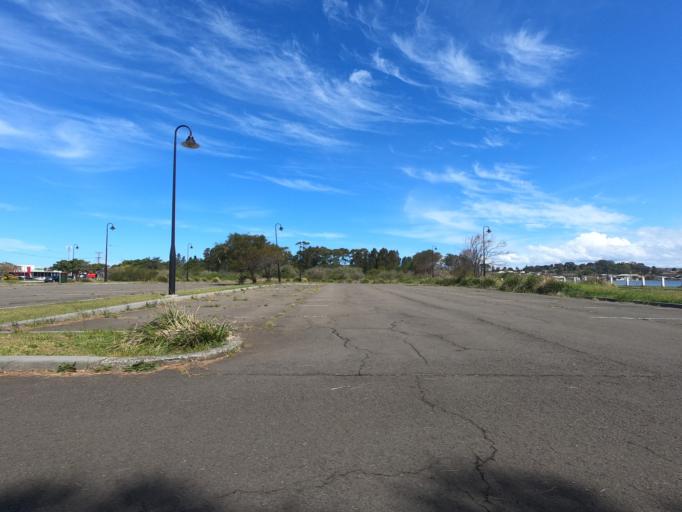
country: AU
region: New South Wales
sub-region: Wollongong
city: Lake Heights
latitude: -34.4943
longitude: 150.8880
